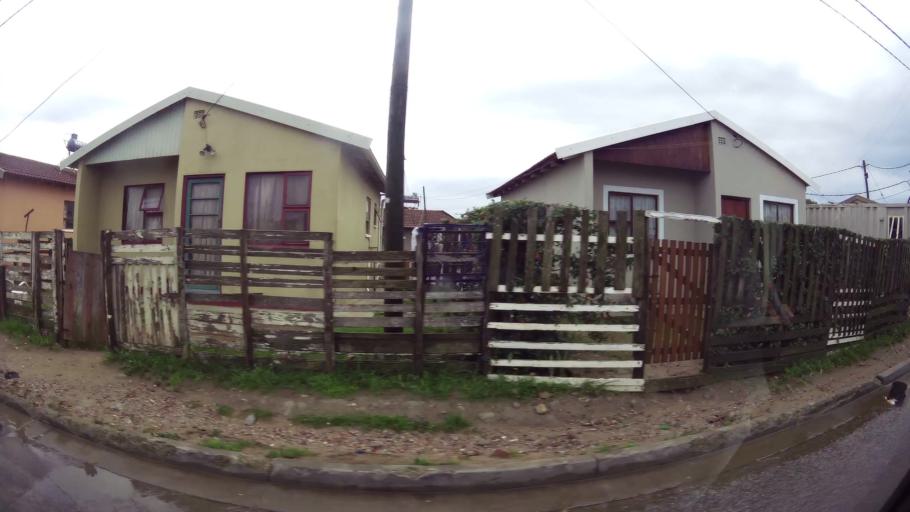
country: ZA
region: Eastern Cape
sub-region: Nelson Mandela Bay Metropolitan Municipality
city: Port Elizabeth
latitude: -33.9910
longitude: 25.5835
